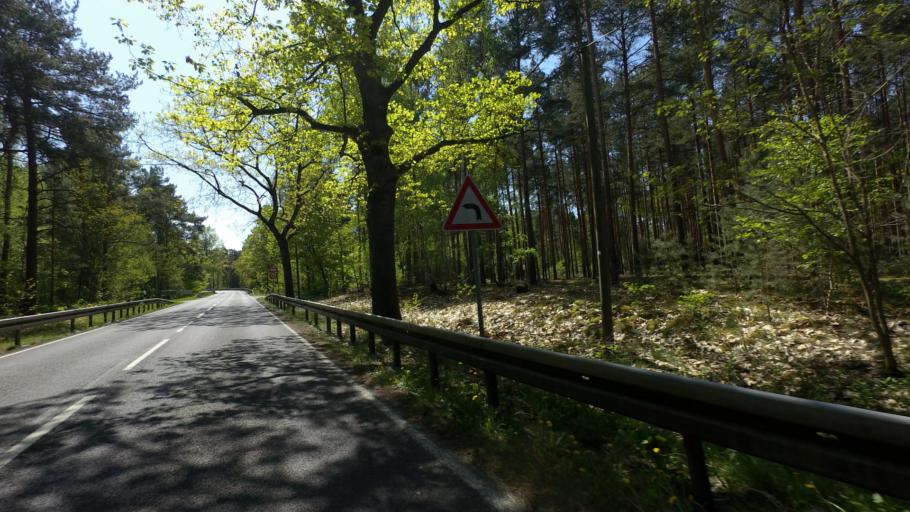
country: DE
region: Brandenburg
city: Gross Koris
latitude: 52.1891
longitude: 13.6983
